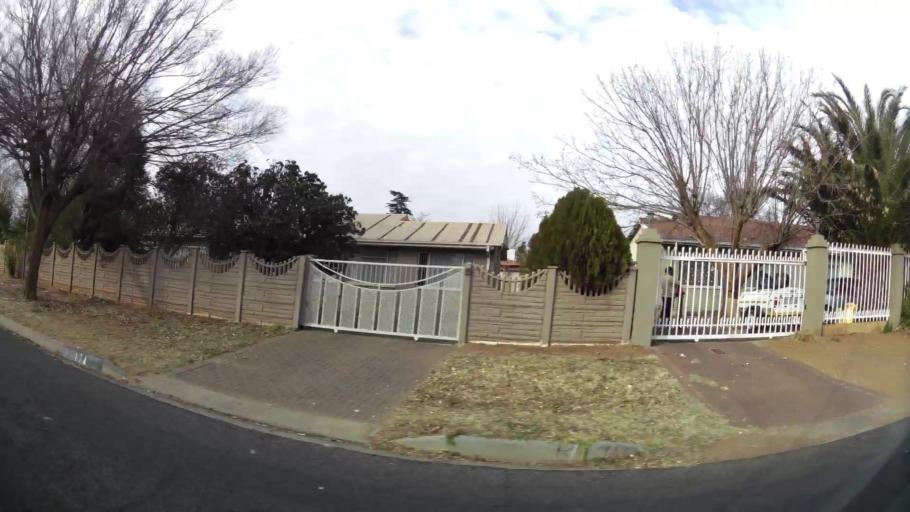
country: ZA
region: Orange Free State
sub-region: Mangaung Metropolitan Municipality
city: Bloemfontein
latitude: -29.1236
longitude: 26.1799
